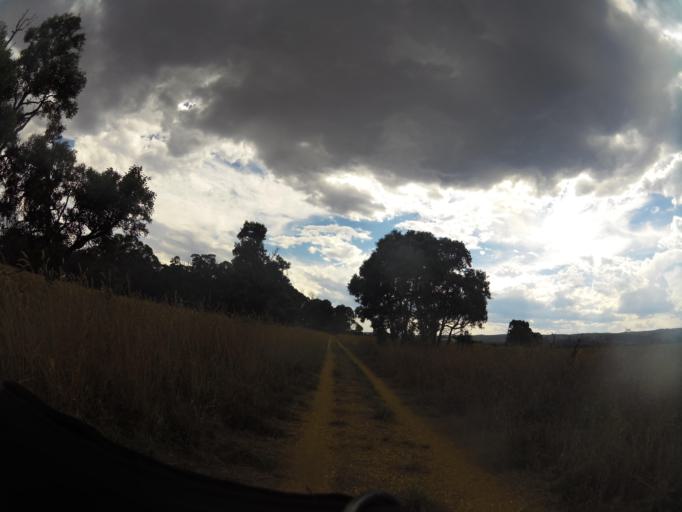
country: AU
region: Victoria
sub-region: Wellington
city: Heyfield
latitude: -38.0166
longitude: 146.6882
